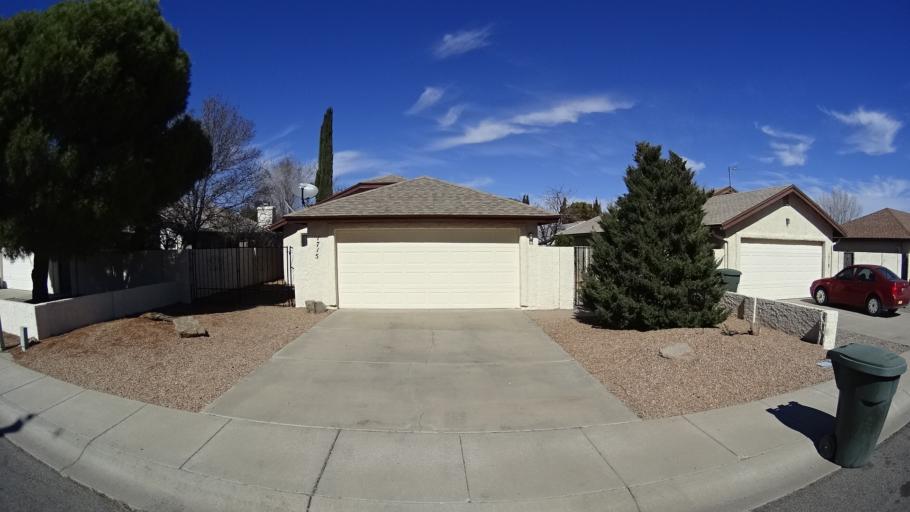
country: US
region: Arizona
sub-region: Mohave County
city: Kingman
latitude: 35.2089
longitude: -114.0393
